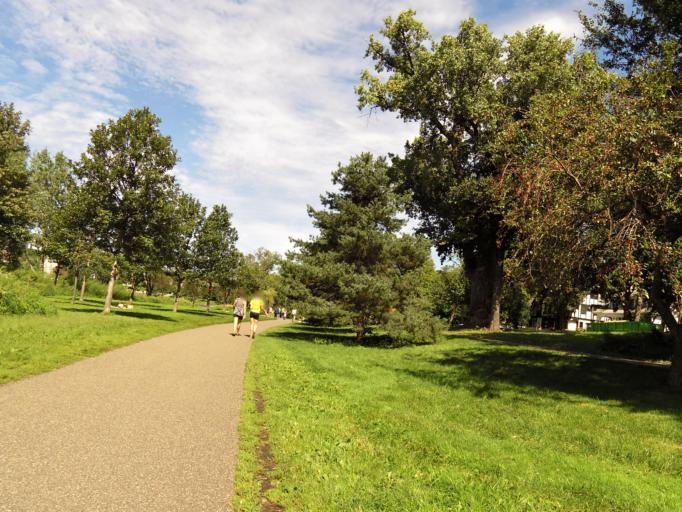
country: US
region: Minnesota
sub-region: Hennepin County
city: Saint Louis Park
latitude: 44.9533
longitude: -93.3027
